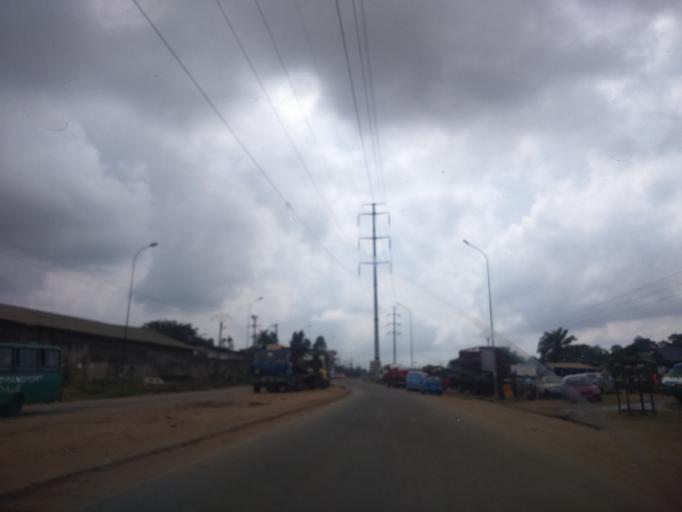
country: CI
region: Lagunes
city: Abobo
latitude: 5.3746
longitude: -4.0775
